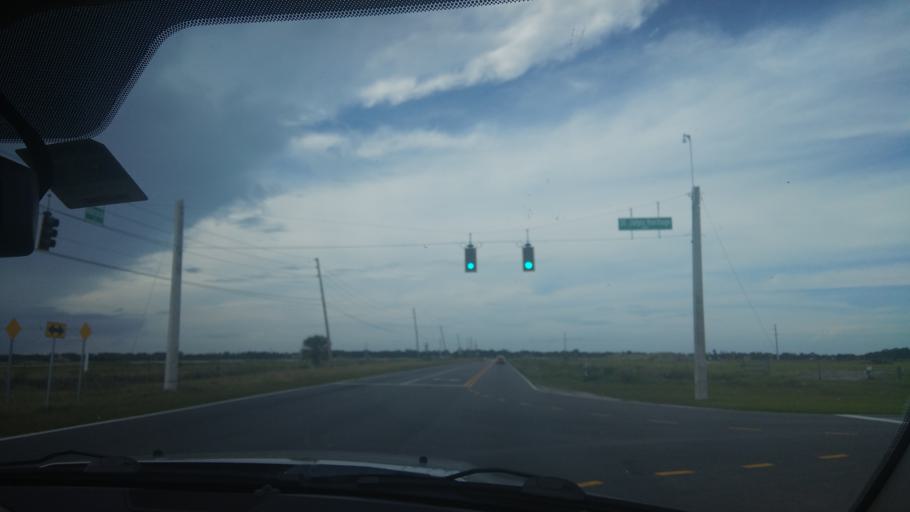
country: US
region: Florida
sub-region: Brevard County
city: Grant-Valkaria
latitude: 27.8968
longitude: -80.6223
